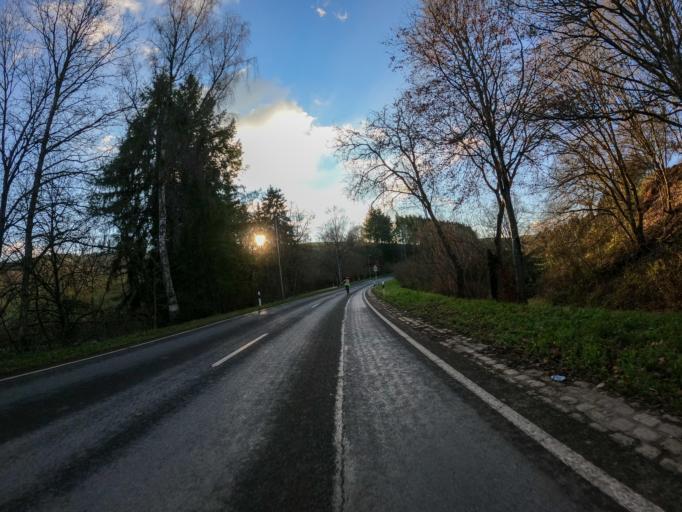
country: LU
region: Diekirch
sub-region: Canton de Wiltz
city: Bavigne
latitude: 49.9637
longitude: 5.8249
